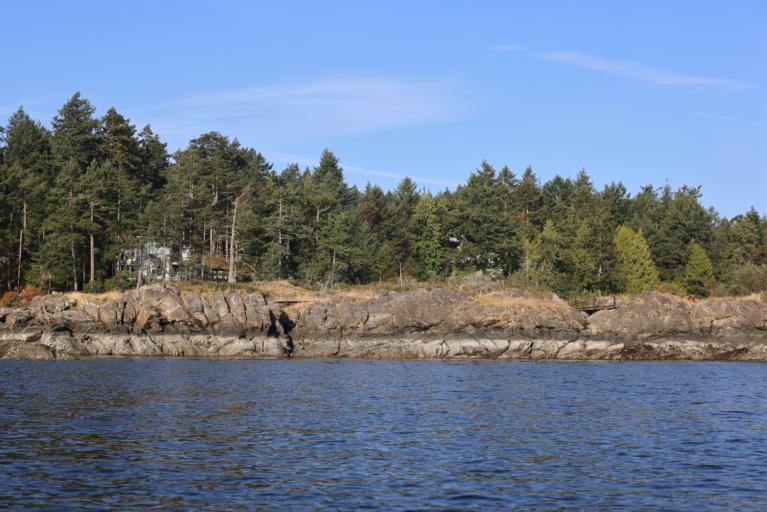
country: CA
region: British Columbia
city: North Saanich
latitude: 48.6787
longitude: -123.3964
